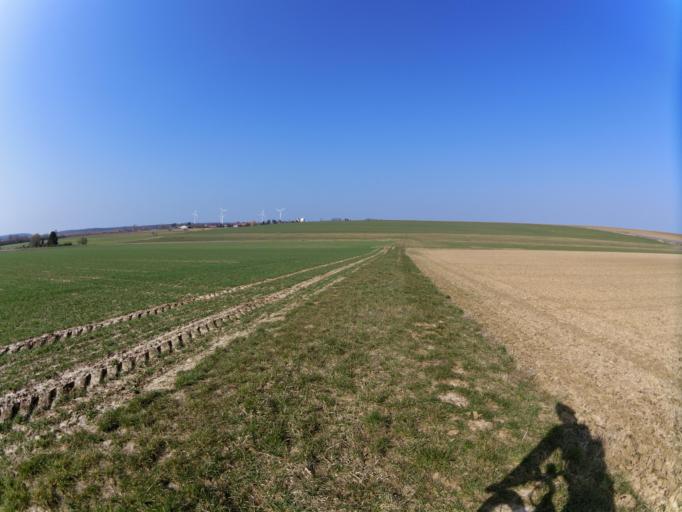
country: DE
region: Bavaria
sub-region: Regierungsbezirk Unterfranken
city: Geroldshausen
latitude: 49.6765
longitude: 9.9117
